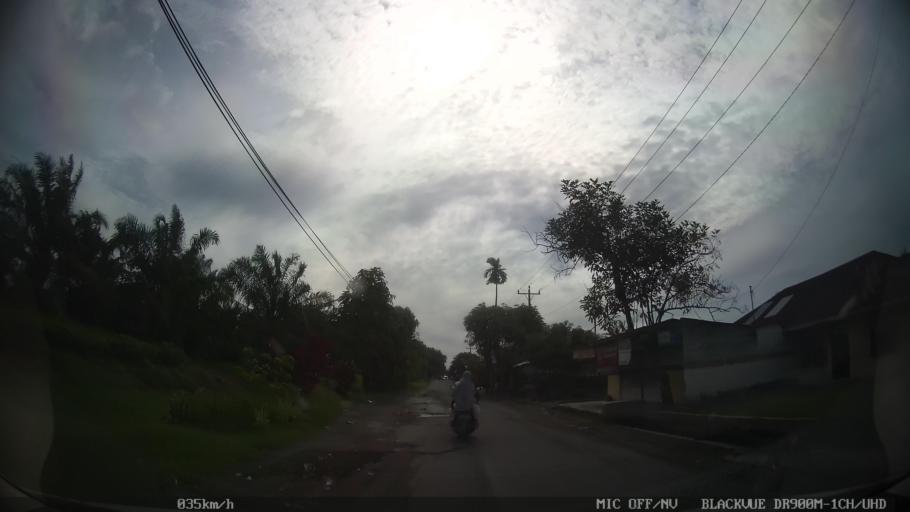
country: ID
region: North Sumatra
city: Medan
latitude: 3.6218
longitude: 98.7100
